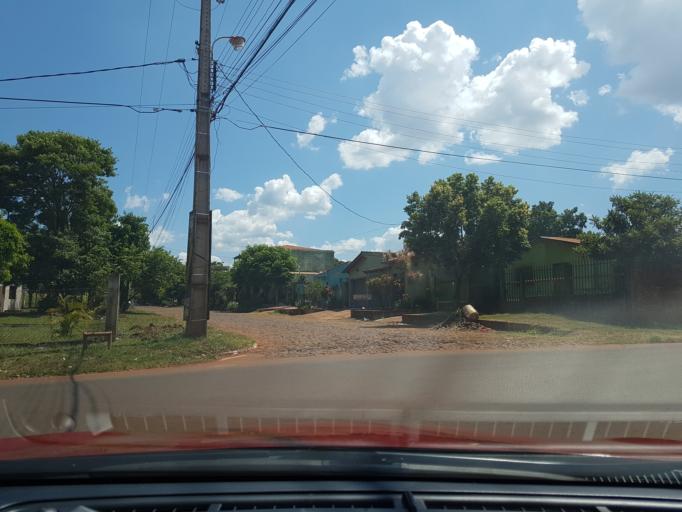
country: PY
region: Alto Parana
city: Ciudad del Este
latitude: -25.4825
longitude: -54.6782
